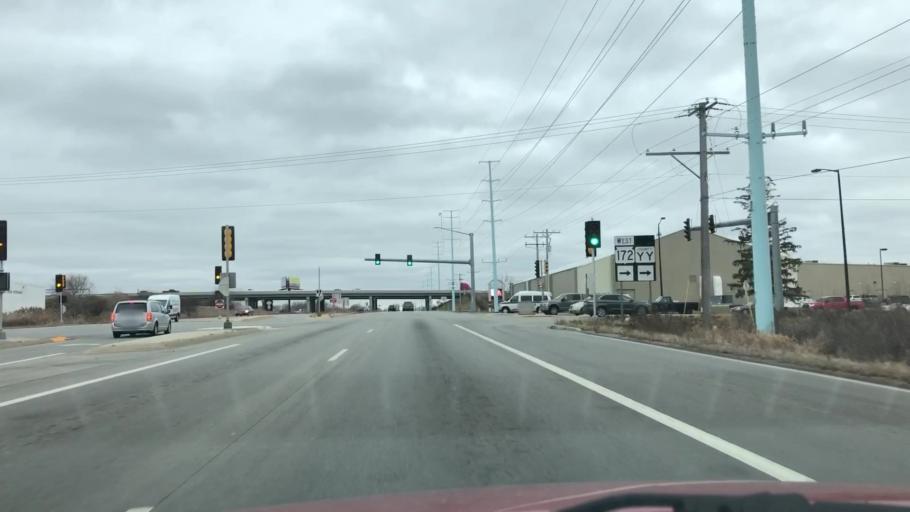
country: US
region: Wisconsin
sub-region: Brown County
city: Ashwaubenon
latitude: 44.4807
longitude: -88.0578
